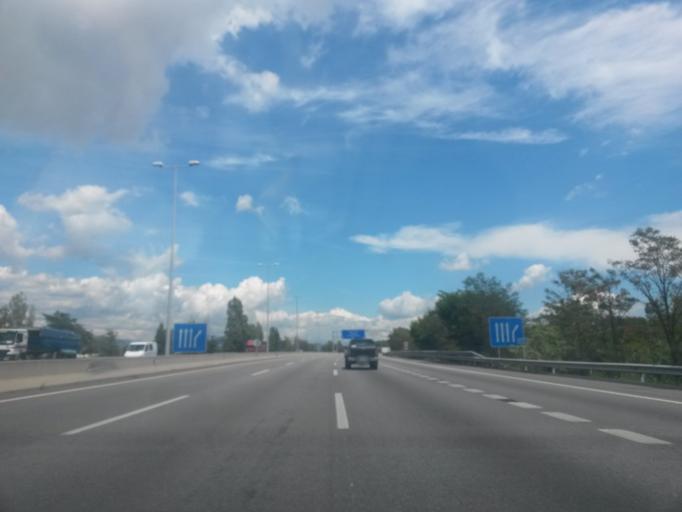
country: ES
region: Catalonia
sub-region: Provincia de Barcelona
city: Montornes del Valles
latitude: 41.5639
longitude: 2.2730
